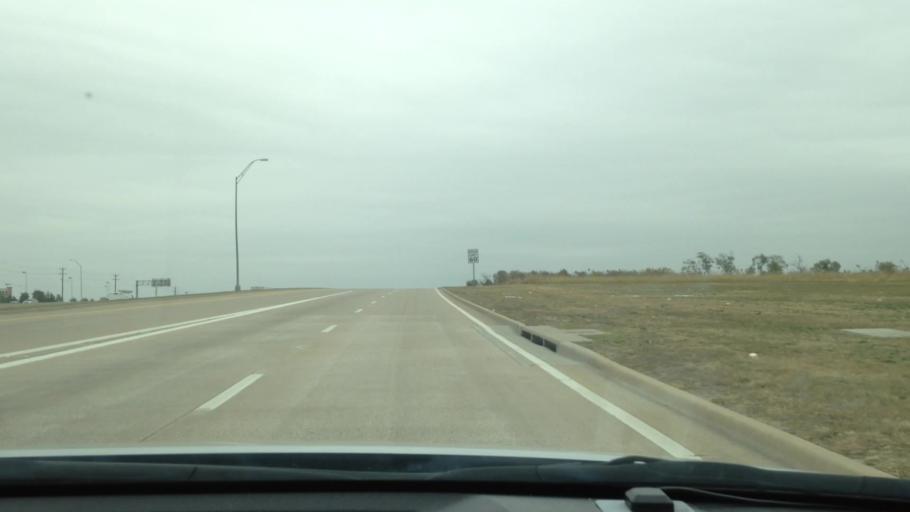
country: US
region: Texas
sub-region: Collin County
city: Allen
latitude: 33.1261
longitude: -96.7284
